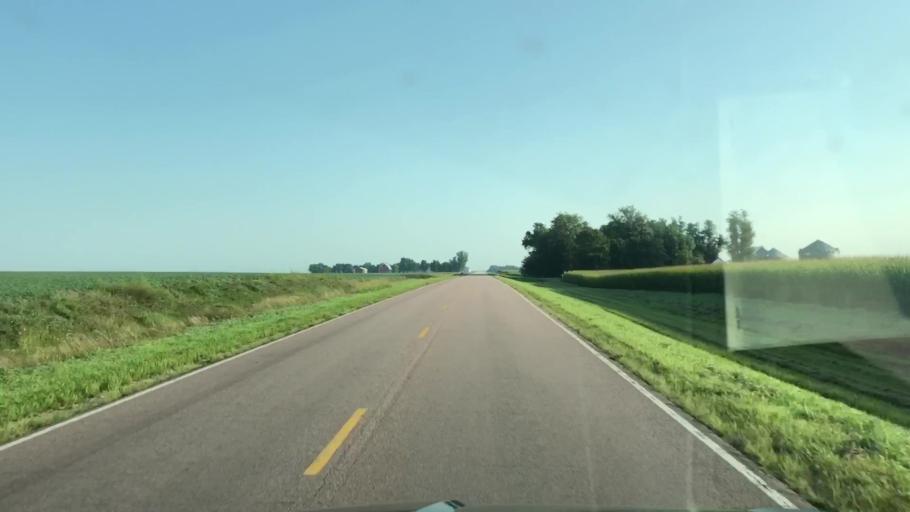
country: US
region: Iowa
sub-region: Lyon County
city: George
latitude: 43.3036
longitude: -95.9993
